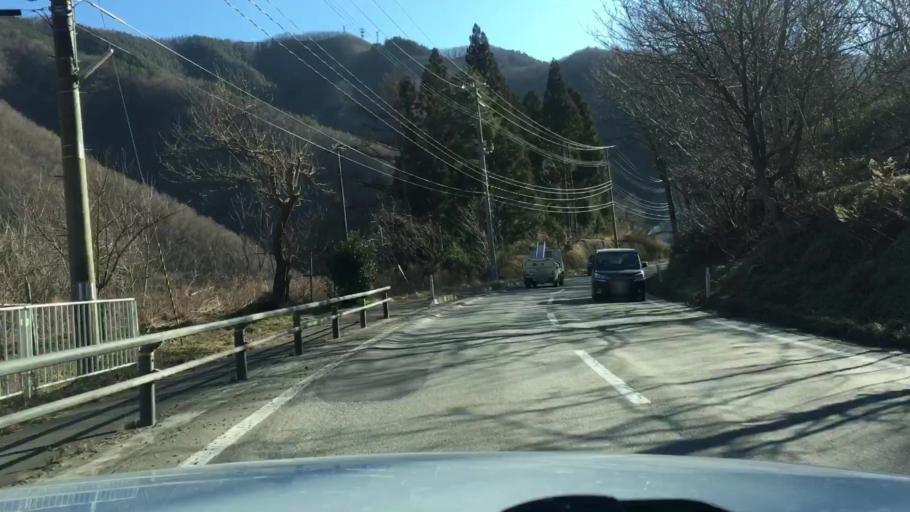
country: JP
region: Iwate
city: Miyako
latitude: 39.6227
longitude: 141.8108
